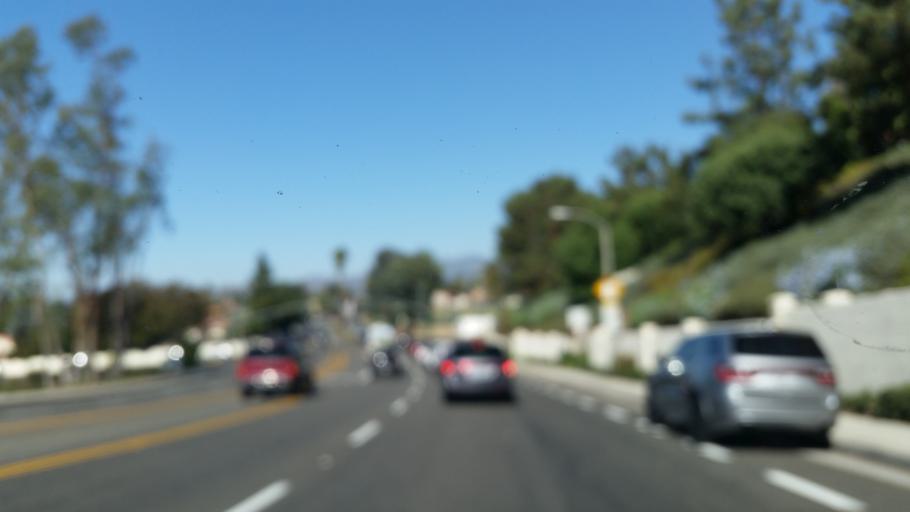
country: US
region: California
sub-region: Orange County
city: Mission Viejo
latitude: 33.5914
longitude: -117.6847
